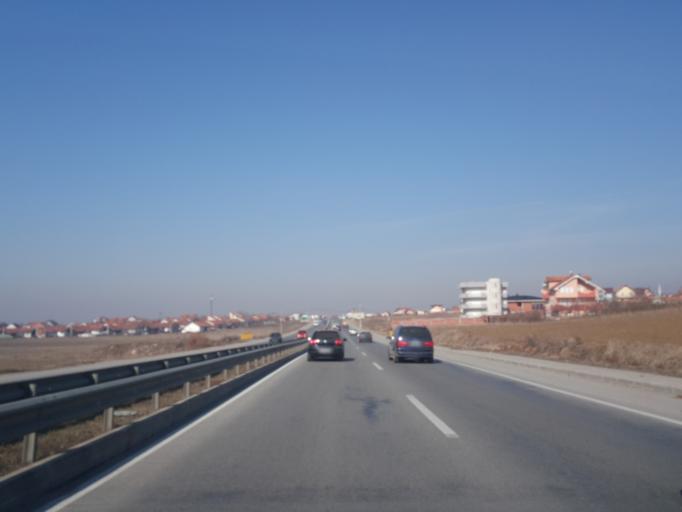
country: XK
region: Pristina
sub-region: Komuna e Obiliqit
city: Obiliq
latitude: 42.7553
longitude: 21.0363
